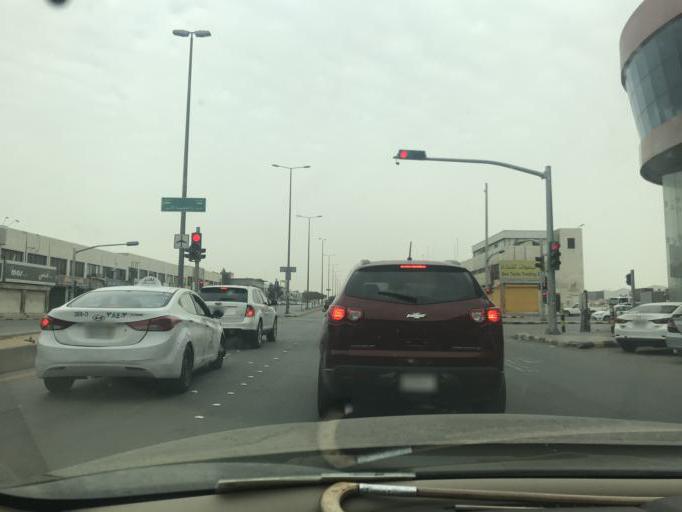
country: SA
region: Ar Riyad
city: Riyadh
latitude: 24.6403
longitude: 46.7498
